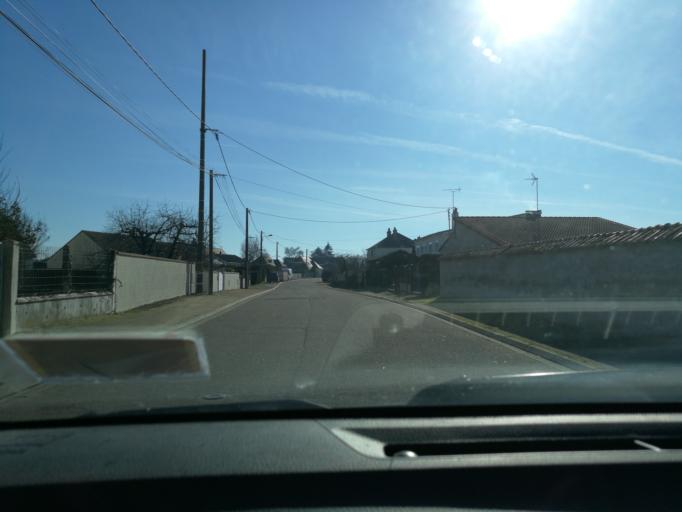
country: FR
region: Centre
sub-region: Departement du Loiret
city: Chaingy
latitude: 47.8855
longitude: 1.7802
